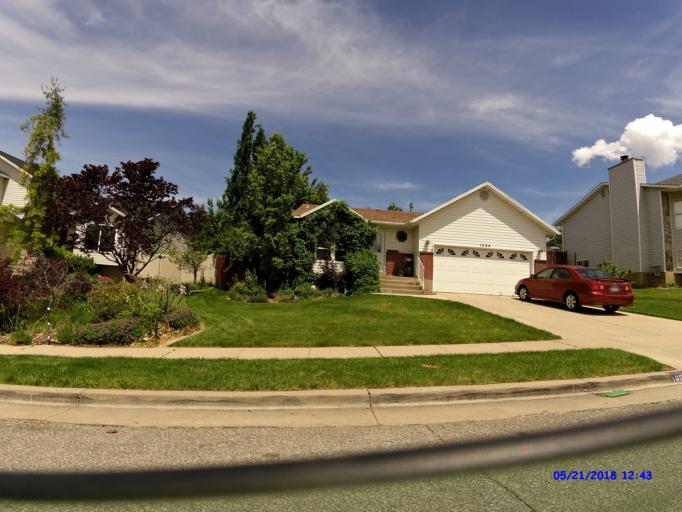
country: US
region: Utah
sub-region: Weber County
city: Washington Terrace
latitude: 41.1721
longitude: -111.9534
